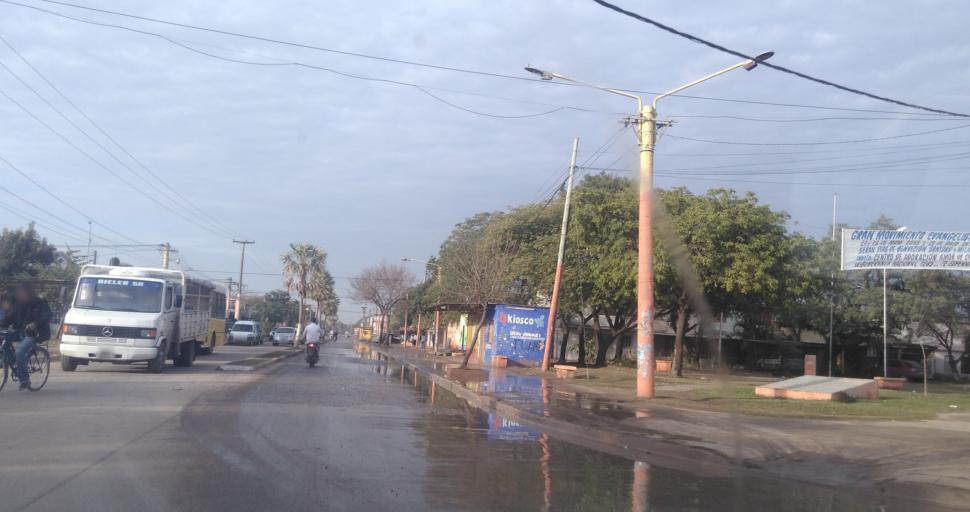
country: AR
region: Chaco
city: Resistencia
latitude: -27.4800
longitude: -58.9899
